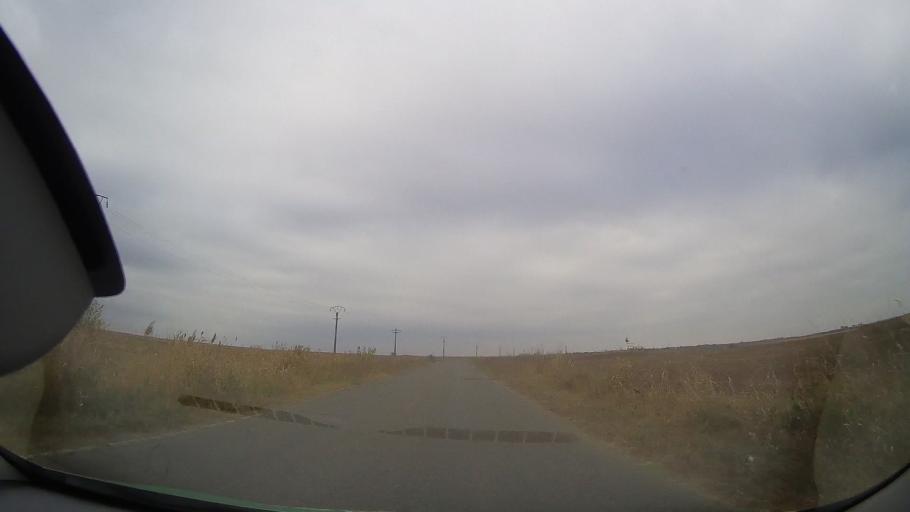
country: RO
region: Buzau
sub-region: Comuna Luciu
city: Luciu
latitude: 44.9672
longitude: 27.1152
